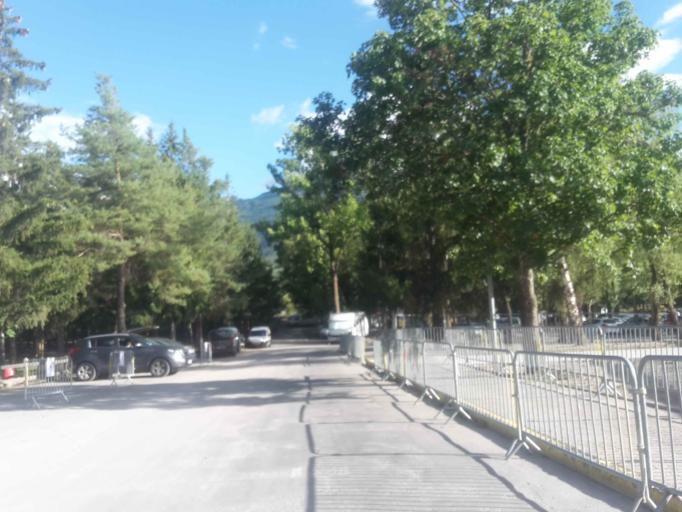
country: FR
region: Provence-Alpes-Cote d'Azur
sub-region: Departement des Hautes-Alpes
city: Embrun
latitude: 44.5509
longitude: 6.4819
